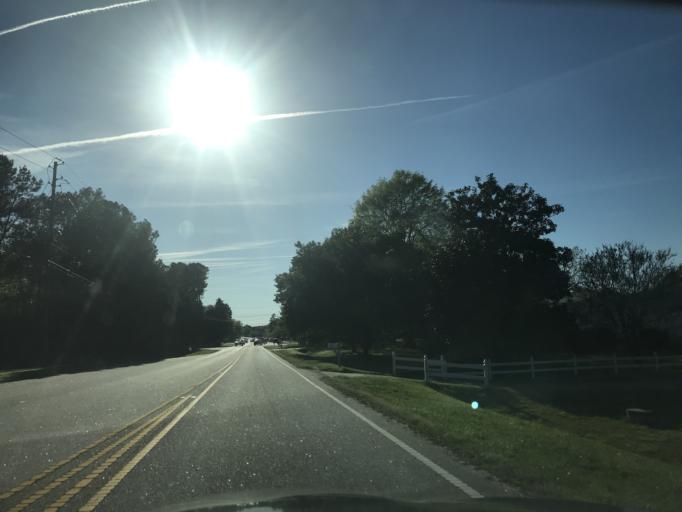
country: US
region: North Carolina
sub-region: Wake County
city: Knightdale
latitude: 35.8560
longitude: -78.5641
